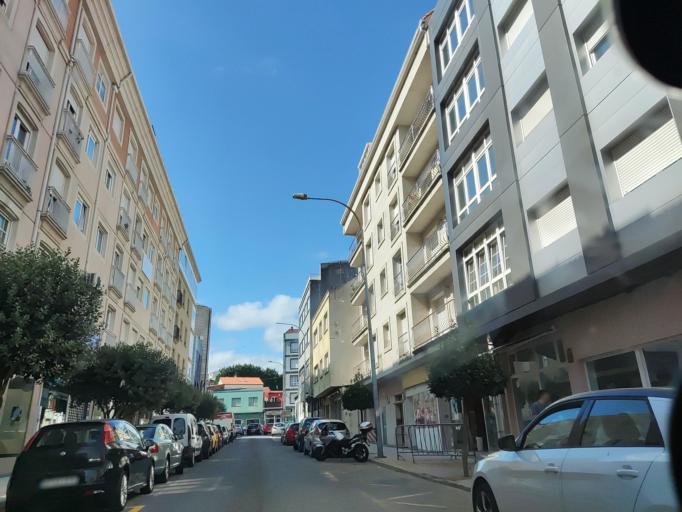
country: ES
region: Galicia
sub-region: Provincia da Coruna
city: Boiro
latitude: 42.6464
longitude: -8.8844
